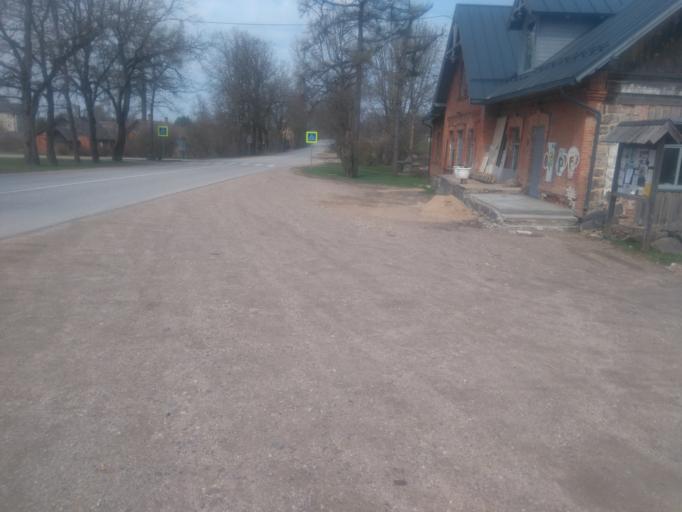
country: LV
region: Vecpiebalga
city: Vecpiebalga
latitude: 57.0208
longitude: 25.8312
